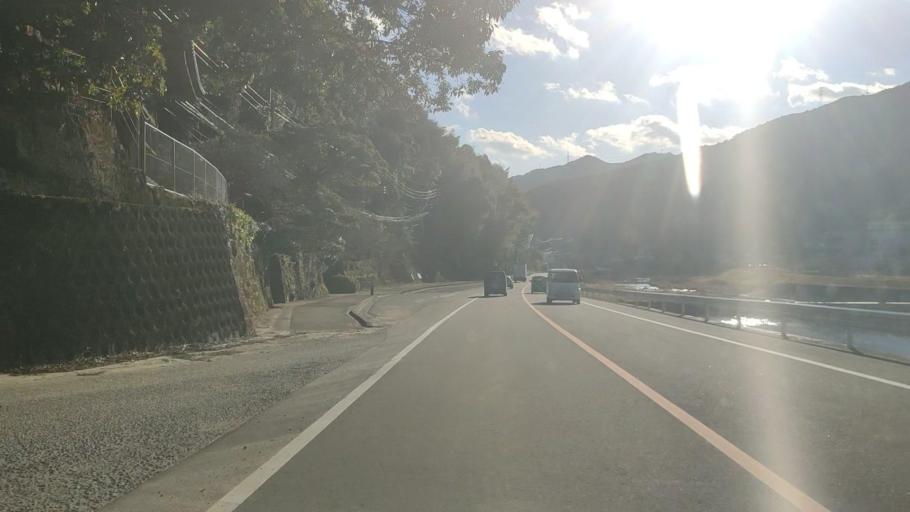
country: JP
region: Saga Prefecture
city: Saga-shi
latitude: 33.3580
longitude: 130.2525
